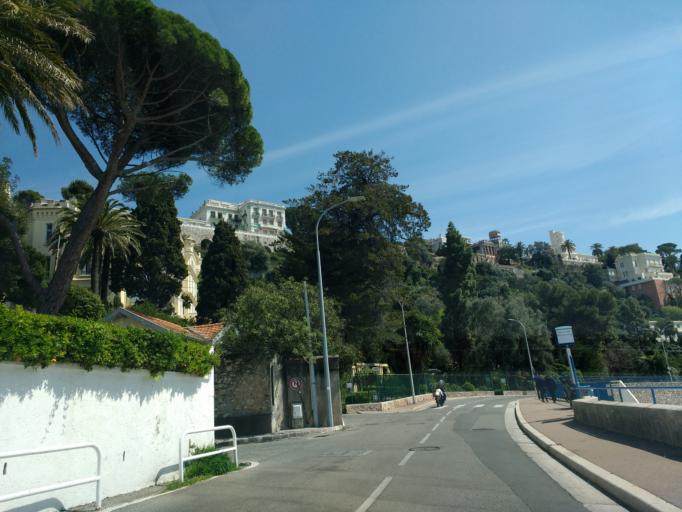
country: FR
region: Provence-Alpes-Cote d'Azur
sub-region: Departement des Alpes-Maritimes
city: Villefranche-sur-Mer
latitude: 43.6911
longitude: 7.2933
